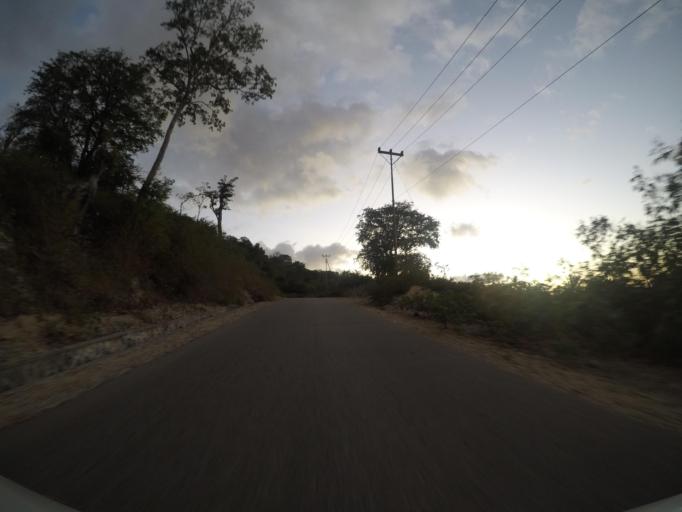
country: TL
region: Lautem
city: Lospalos
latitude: -8.3646
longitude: 127.0533
